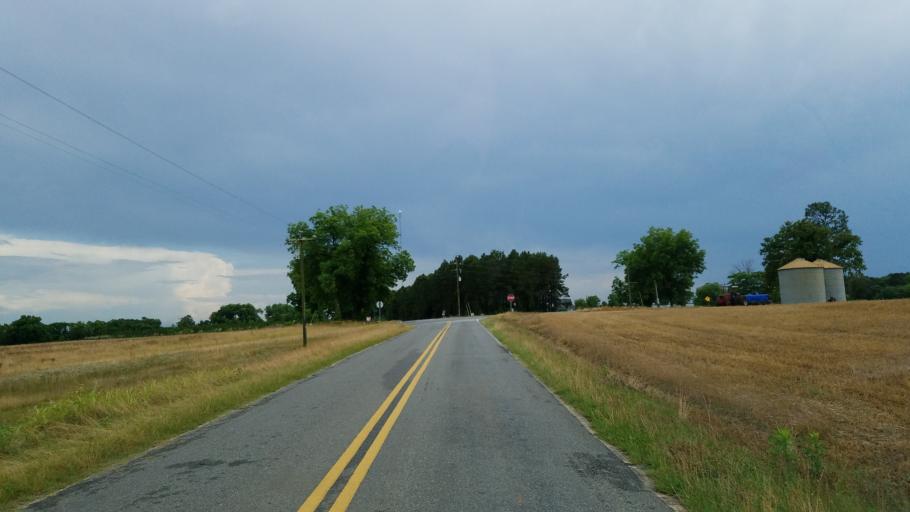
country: US
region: Georgia
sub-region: Dooly County
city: Unadilla
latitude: 32.2476
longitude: -83.7975
